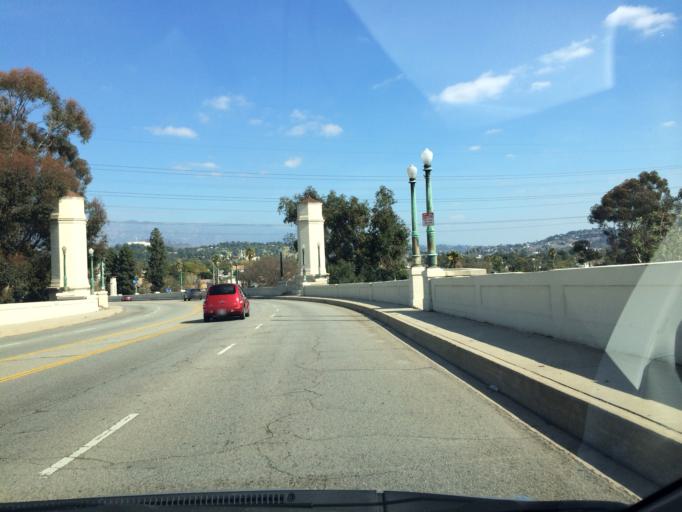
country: US
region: California
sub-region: Los Angeles County
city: Silver Lake
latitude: 34.1125
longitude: -118.2668
